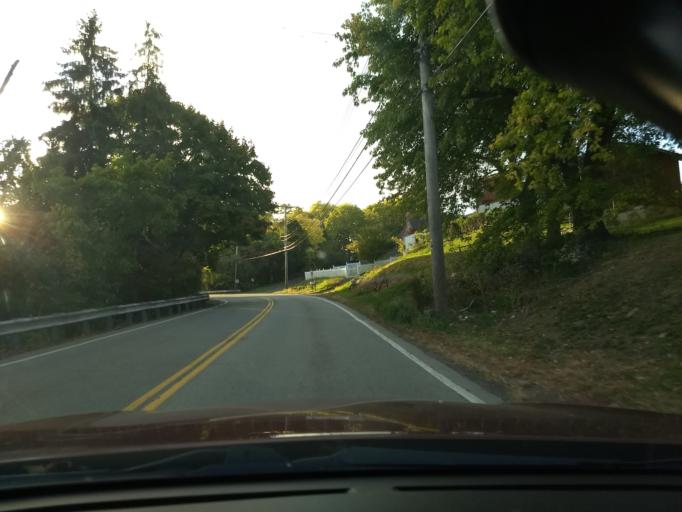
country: US
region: Pennsylvania
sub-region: Allegheny County
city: Dravosburg
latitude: 40.3524
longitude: -79.9051
